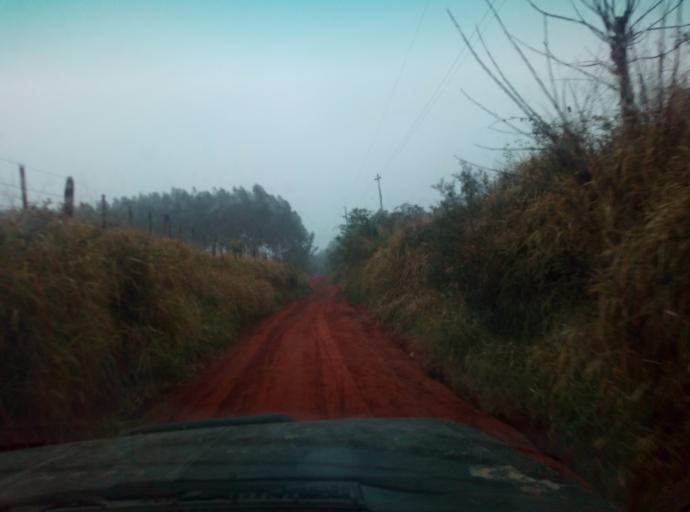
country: PY
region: Caaguazu
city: Doctor Cecilio Baez
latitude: -25.1623
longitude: -56.2620
